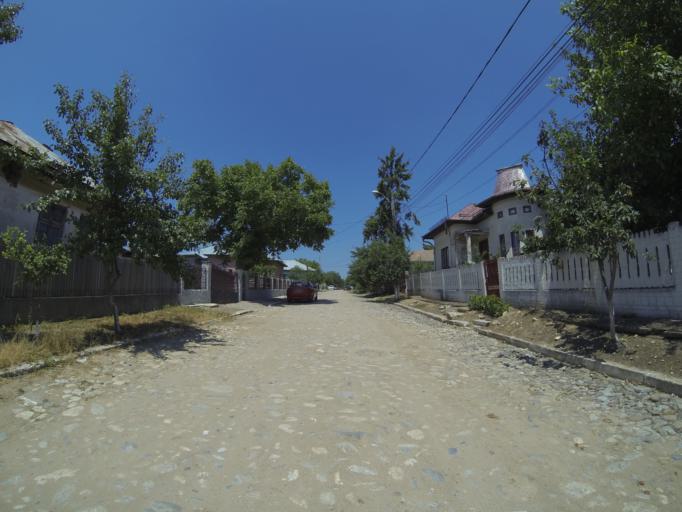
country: RO
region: Dolj
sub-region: Comuna Segarcea
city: Segarcea
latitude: 44.0901
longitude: 23.7502
